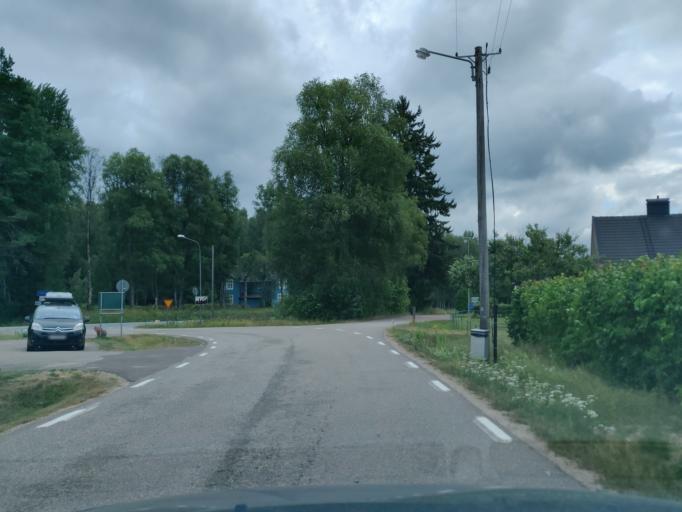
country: SE
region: Vaermland
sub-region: Munkfors Kommun
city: Munkfors
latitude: 59.8742
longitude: 13.5598
